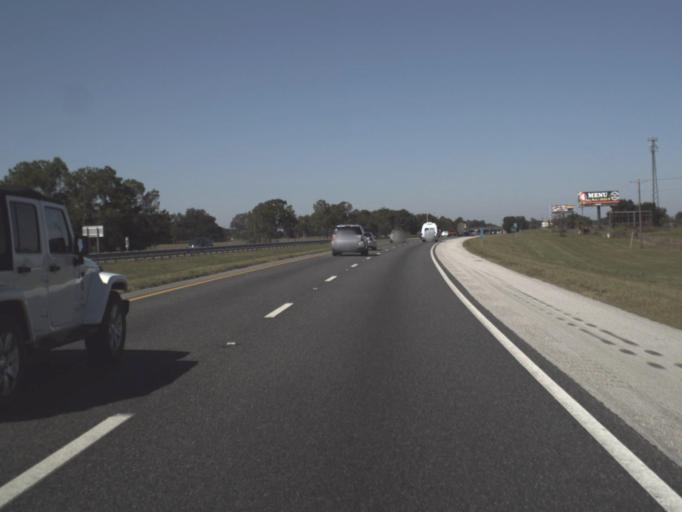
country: US
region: Florida
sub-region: Sumter County
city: Wildwood
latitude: 28.7922
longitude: -81.9909
